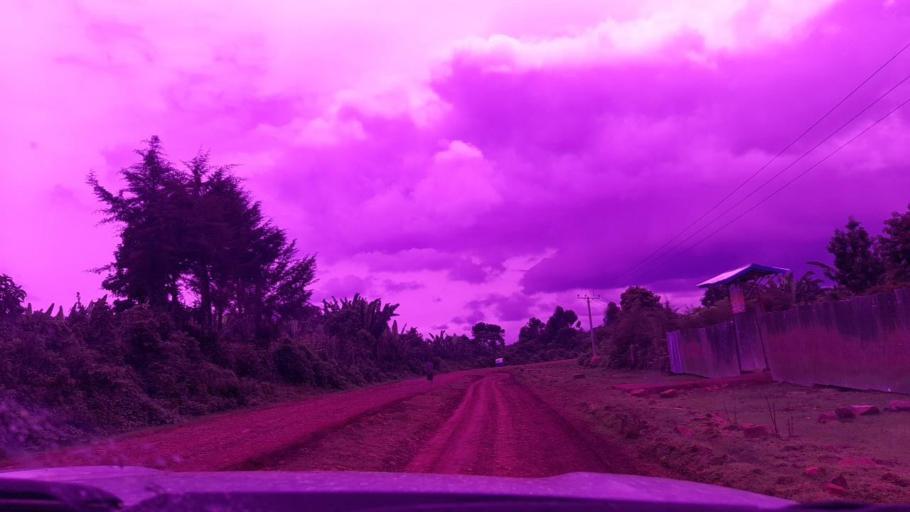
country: ET
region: Southern Nations, Nationalities, and People's Region
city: Tippi
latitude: 7.5745
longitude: 35.6364
